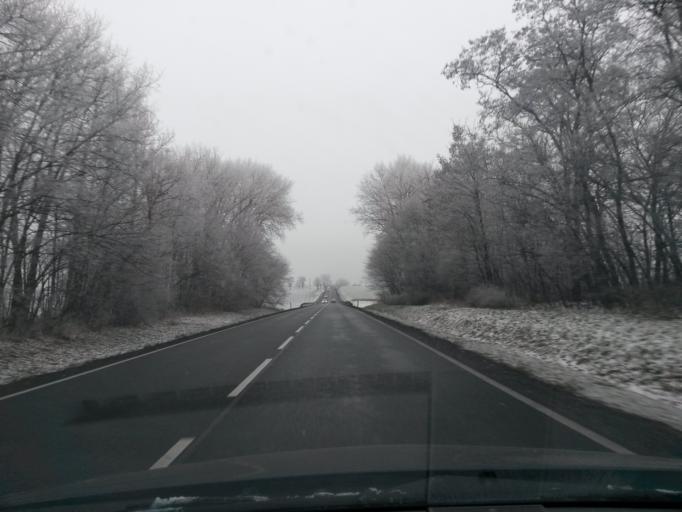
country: PL
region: Kujawsko-Pomorskie
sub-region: Powiat mogilenski
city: Strzelno
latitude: 52.6608
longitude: 18.1910
